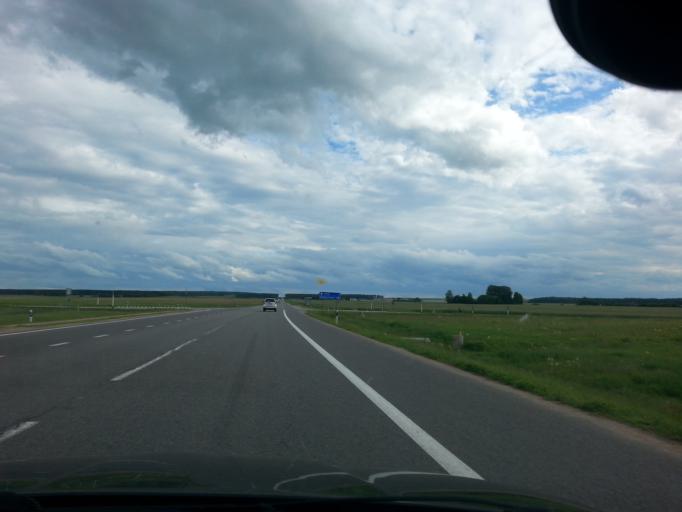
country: BY
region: Grodnenskaya
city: Astravyets
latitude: 54.7348
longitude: 26.0872
